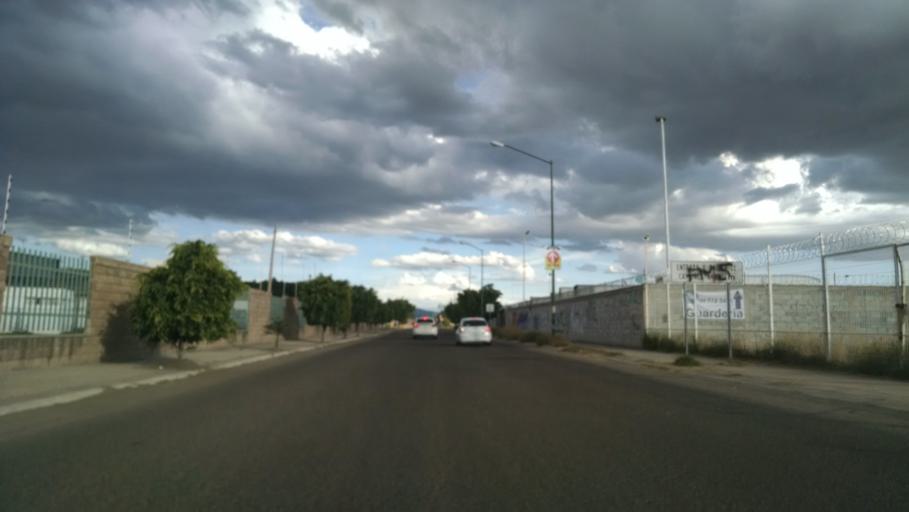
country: MX
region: Guanajuato
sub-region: Leon
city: Ladrilleras del Refugio
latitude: 21.0630
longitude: -101.5836
